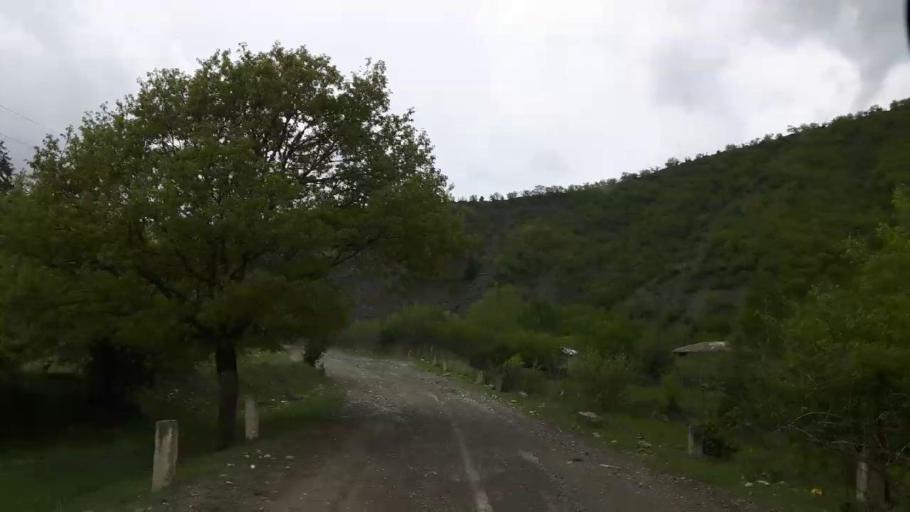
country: GE
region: Shida Kartli
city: Gori
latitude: 41.8692
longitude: 43.9841
